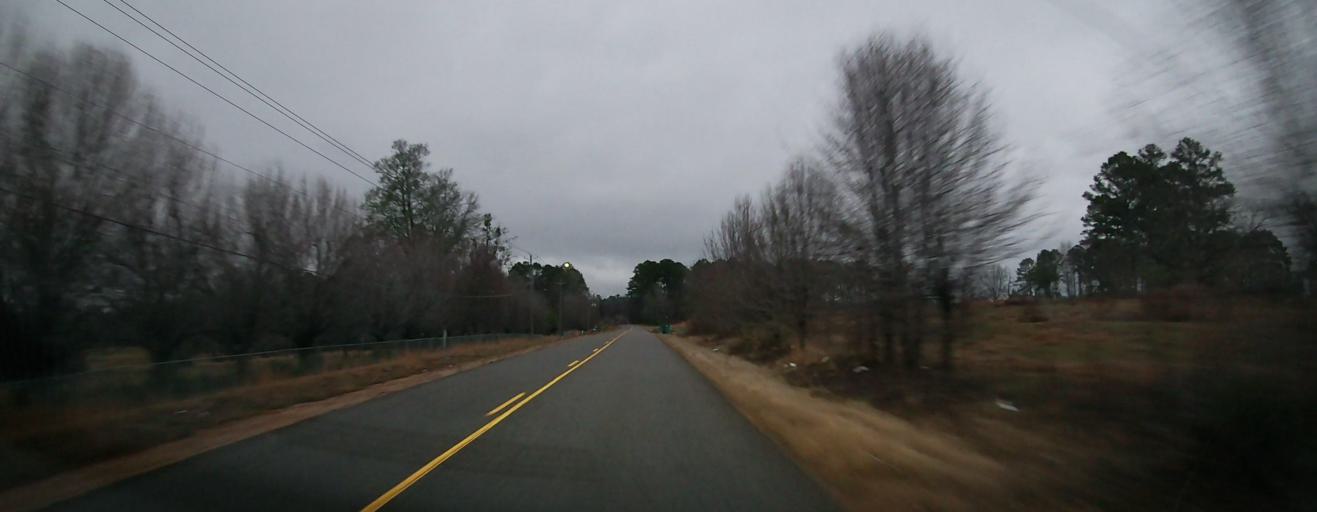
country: US
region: Alabama
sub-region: Tuscaloosa County
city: Vance
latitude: 33.1575
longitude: -87.2299
